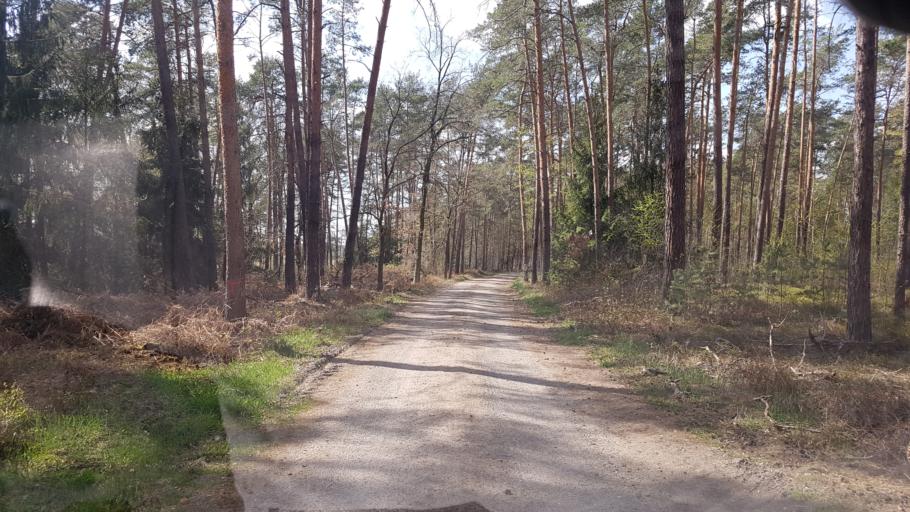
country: DE
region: Brandenburg
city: Ruckersdorf
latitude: 51.5500
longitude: 13.6423
